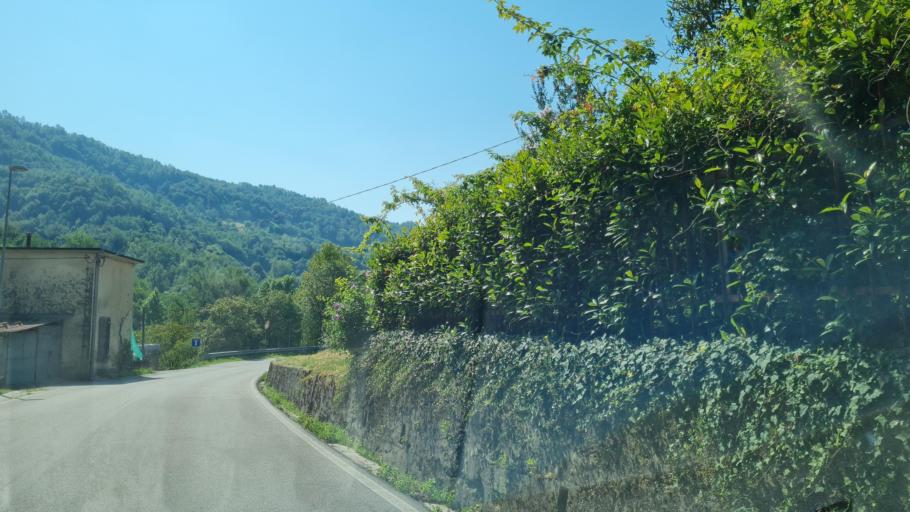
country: IT
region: Veneto
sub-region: Provincia di Vicenza
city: Salcedo
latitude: 45.7624
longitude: 11.5930
